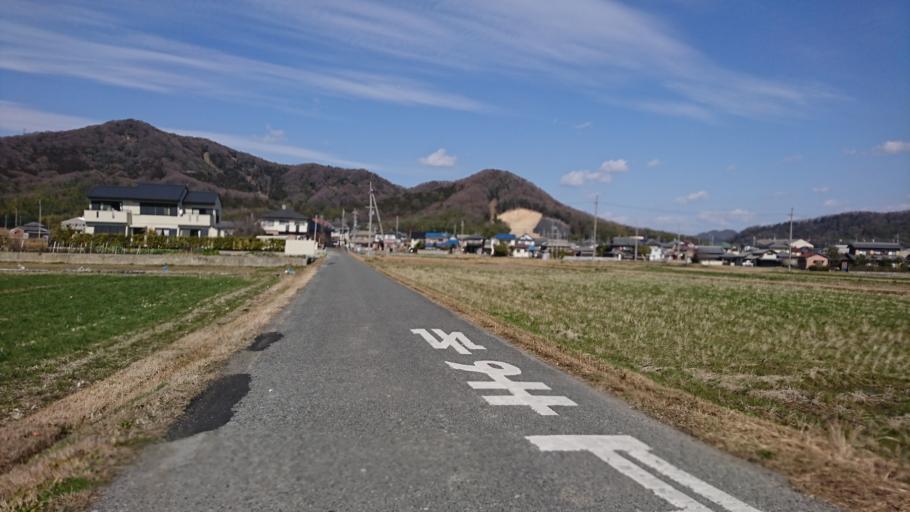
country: JP
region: Hyogo
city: Kakogawacho-honmachi
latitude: 34.8210
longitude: 134.8073
